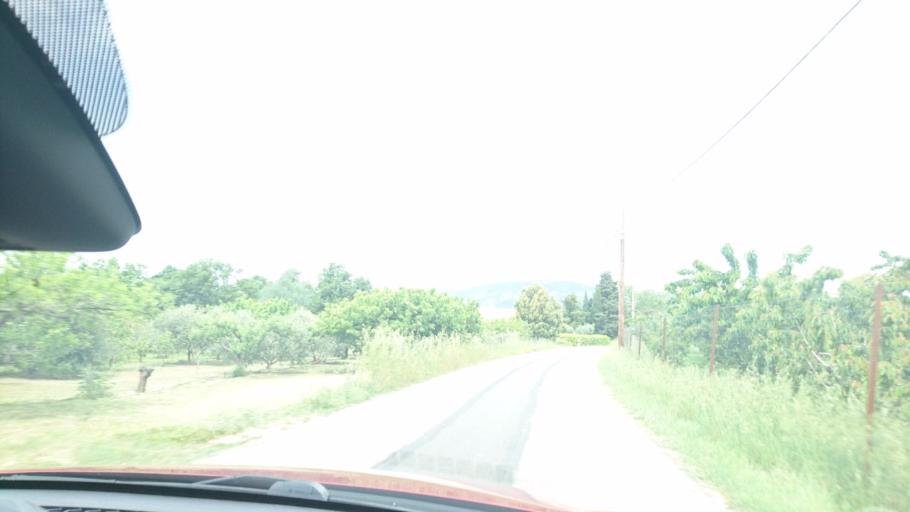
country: FR
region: Provence-Alpes-Cote d'Azur
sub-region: Departement du Vaucluse
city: Villes-sur-Auzon
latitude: 44.0703
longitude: 5.2327
